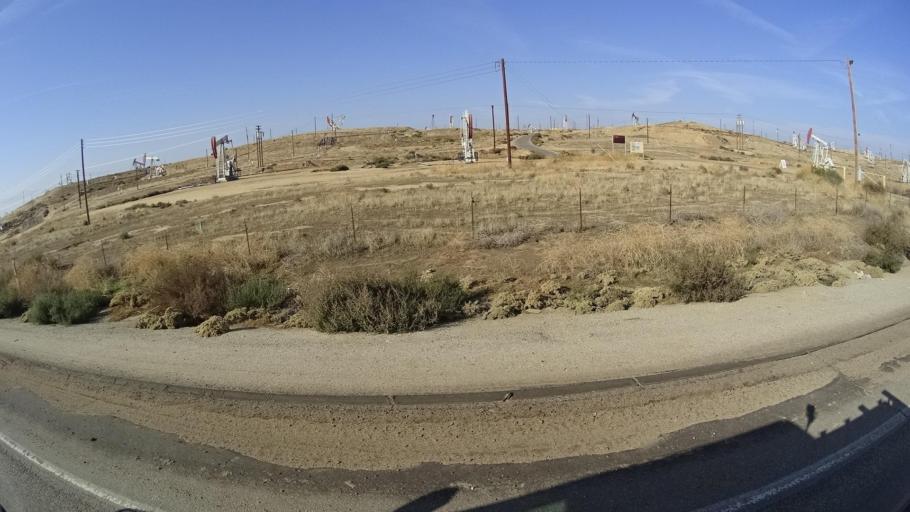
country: US
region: California
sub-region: Kern County
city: Oildale
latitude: 35.4667
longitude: -119.0251
